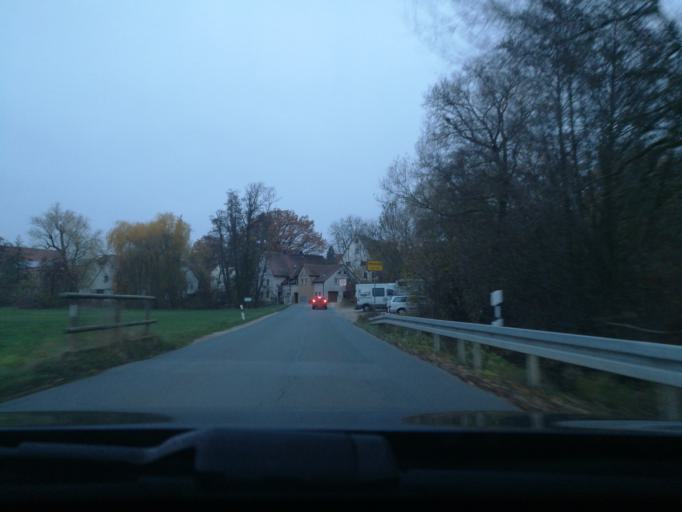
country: DE
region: Bavaria
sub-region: Regierungsbezirk Mittelfranken
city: Obermichelbach
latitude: 49.5079
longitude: 10.9386
